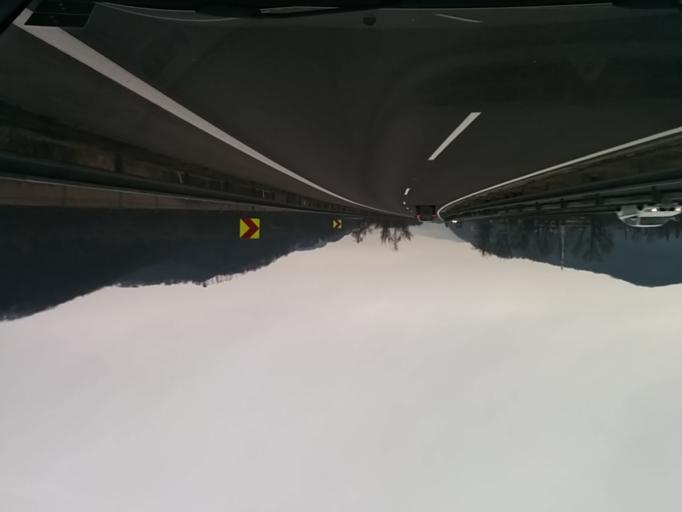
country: SK
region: Banskobystricky
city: Zarnovica
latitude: 48.4786
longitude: 18.7299
